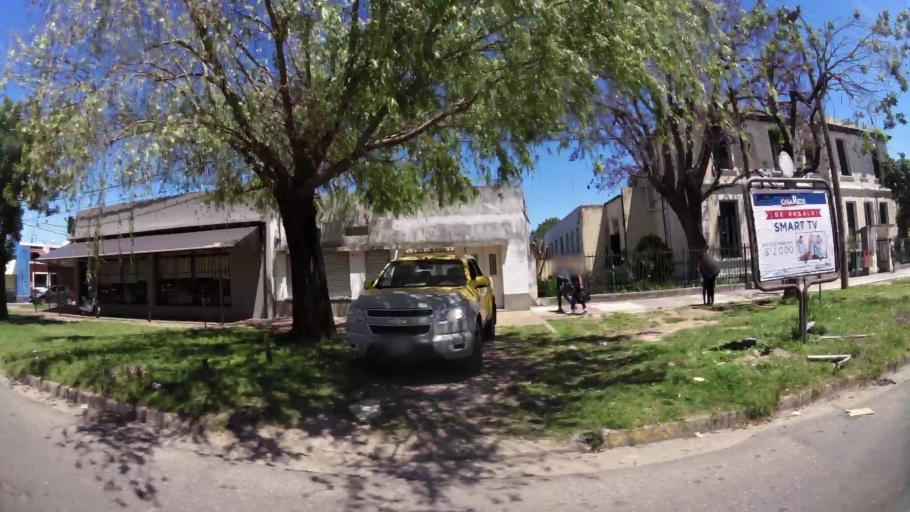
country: AR
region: Santa Fe
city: Santa Fe de la Vera Cruz
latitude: -31.6270
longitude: -60.7138
